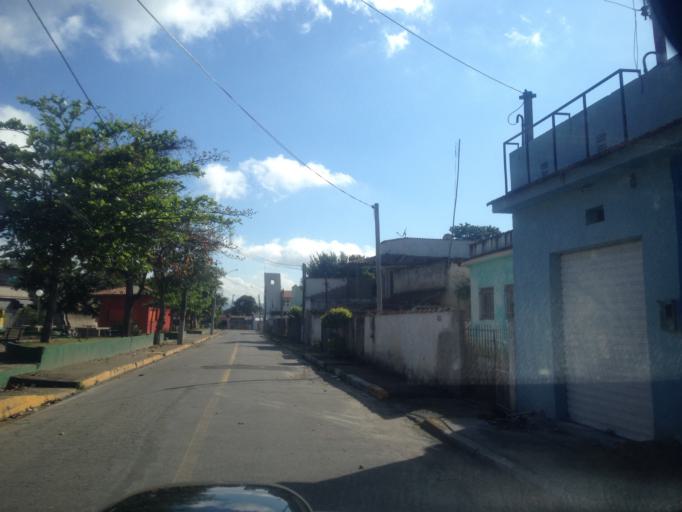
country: BR
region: Rio de Janeiro
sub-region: Porto Real
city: Porto Real
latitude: -22.4441
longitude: -44.3123
